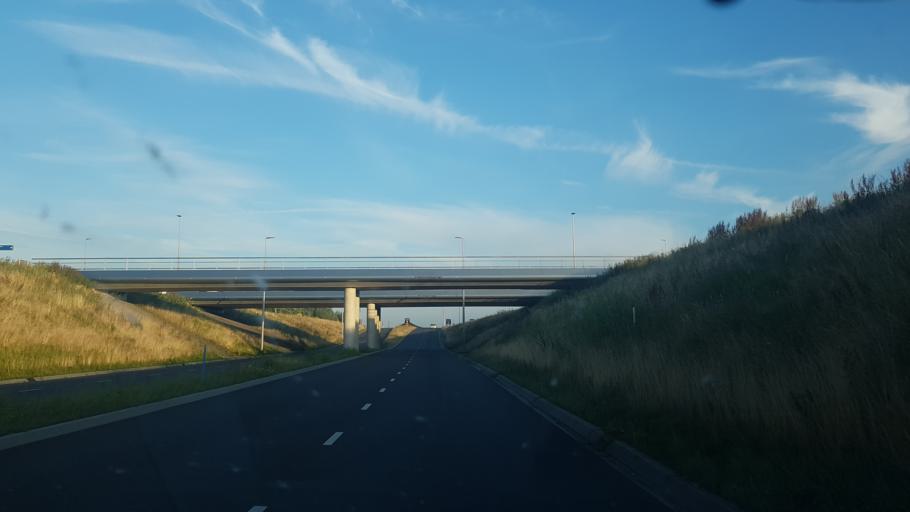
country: NL
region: Friesland
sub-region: Gemeente Leeuwarden
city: Huizum
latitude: 53.1810
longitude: 5.8210
